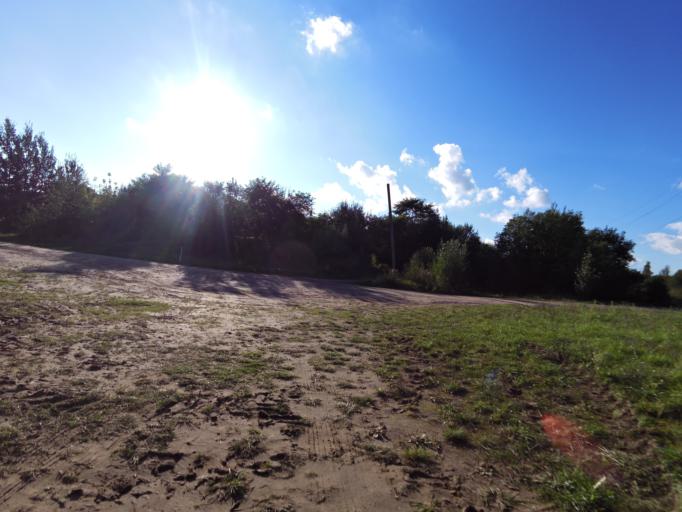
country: LT
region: Vilnius County
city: Justiniskes
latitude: 54.7226
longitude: 25.2279
